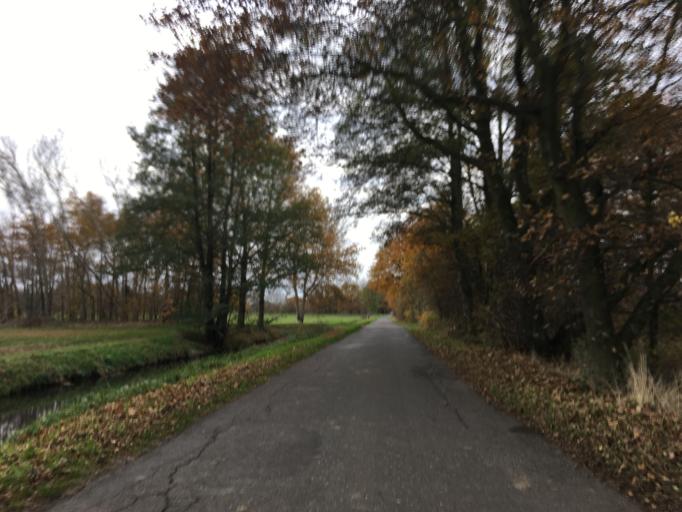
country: DE
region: Brandenburg
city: Werben
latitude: 51.8399
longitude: 14.1864
